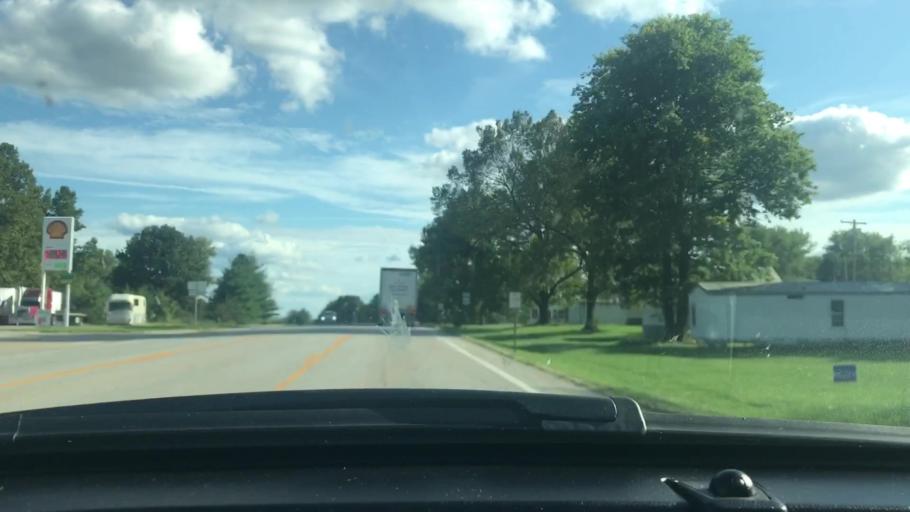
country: US
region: Missouri
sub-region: Oregon County
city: Thayer
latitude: 36.5948
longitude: -91.6439
